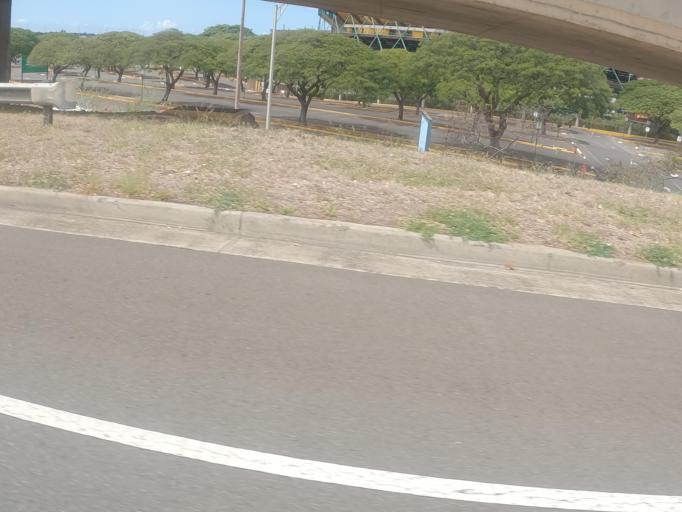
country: US
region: Hawaii
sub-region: Honolulu County
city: Halawa
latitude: 21.3745
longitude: -157.9277
